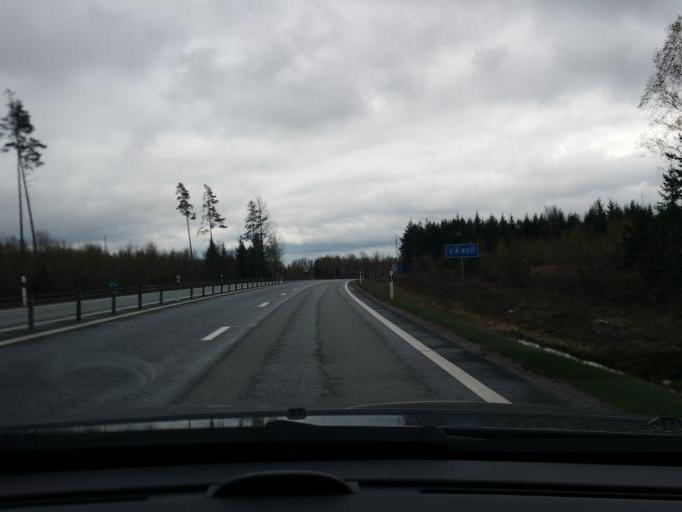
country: SE
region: Kronoberg
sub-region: Vaxjo Kommun
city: Vaexjoe
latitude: 56.9050
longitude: 14.7282
